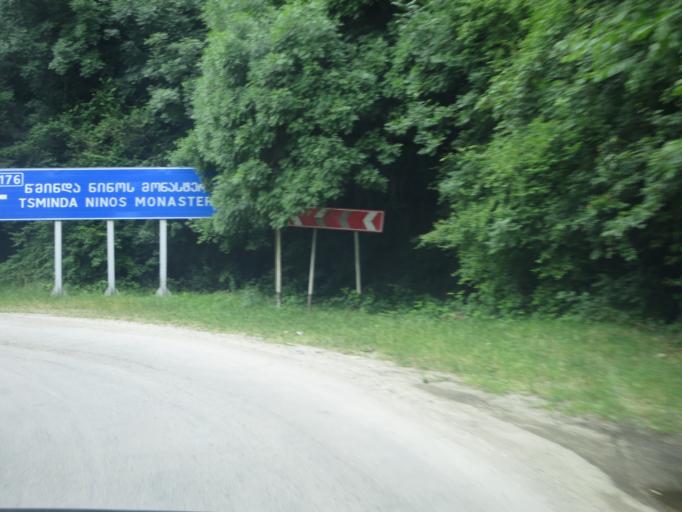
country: GE
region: Kakheti
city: Sighnaghi
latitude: 41.6111
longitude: 45.9228
